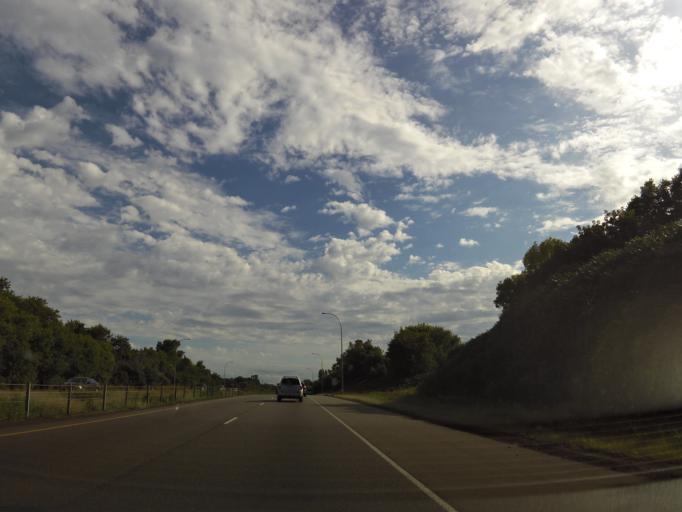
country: US
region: Minnesota
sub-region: Hennepin County
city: New Hope
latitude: 45.0757
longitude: -93.4019
